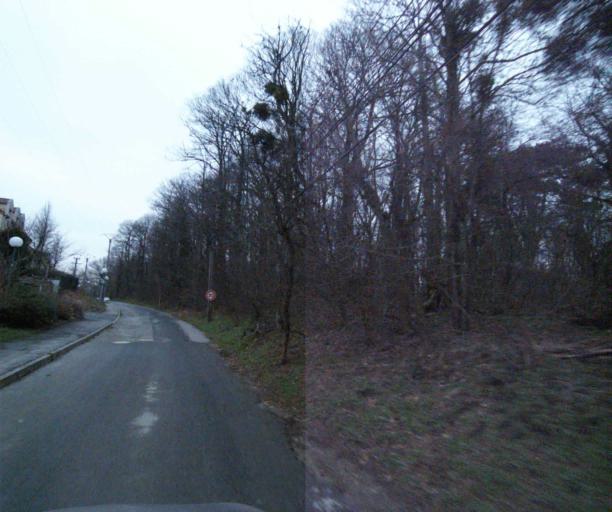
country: FR
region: Ile-de-France
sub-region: Departement de Seine-et-Marne
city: Dammartin-en-Goele
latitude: 49.0587
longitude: 2.6685
